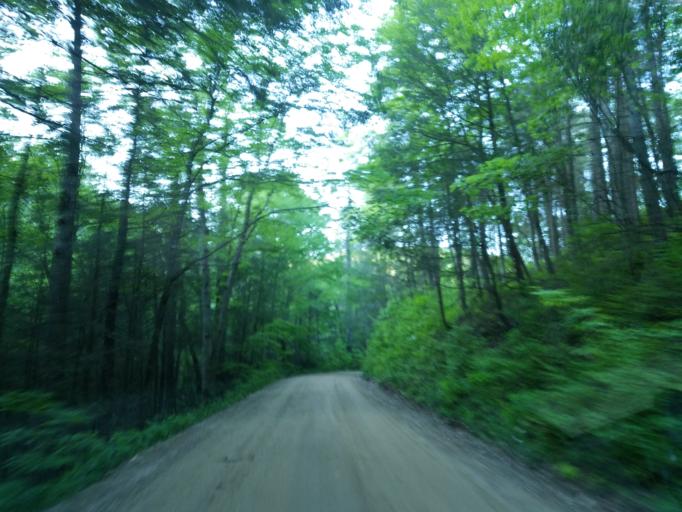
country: US
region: Georgia
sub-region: Lumpkin County
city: Dahlonega
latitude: 34.6954
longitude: -84.1429
